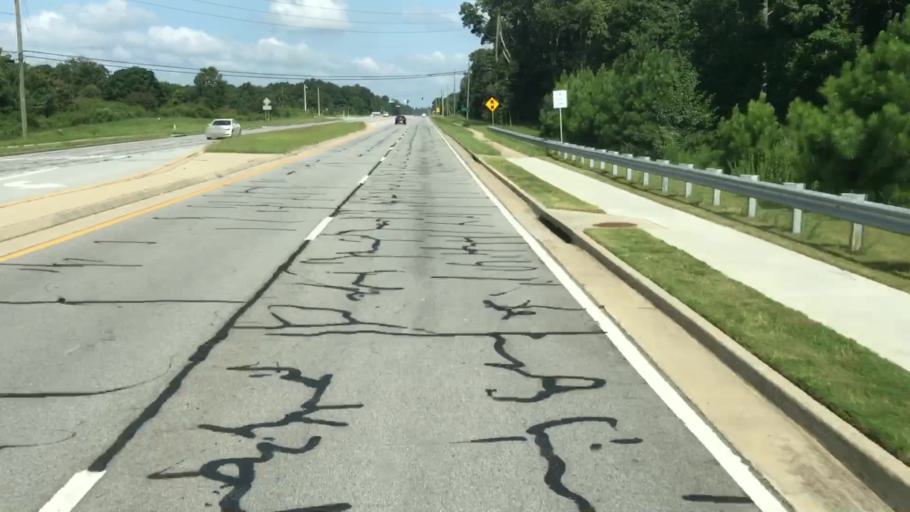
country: US
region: Georgia
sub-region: Walton County
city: Loganville
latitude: 33.8707
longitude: -83.9165
